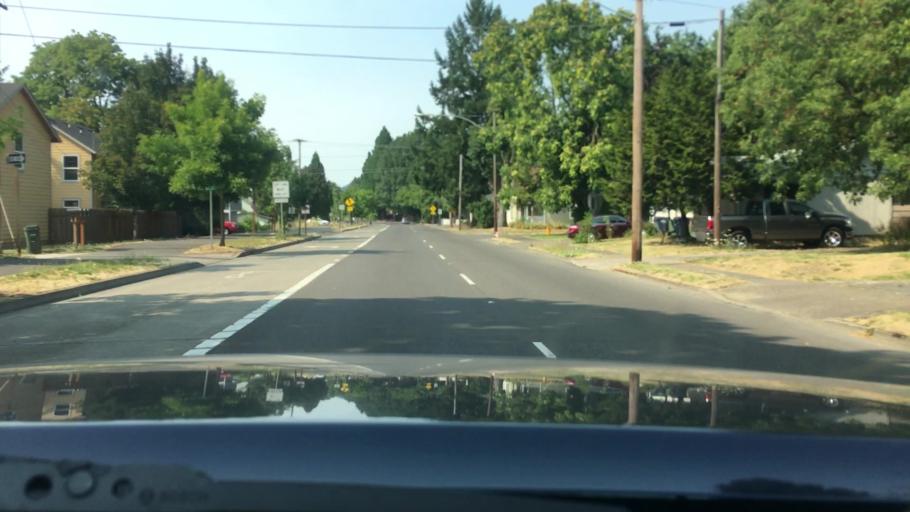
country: US
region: Oregon
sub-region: Lane County
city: Springfield
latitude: 44.0490
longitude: -123.0220
